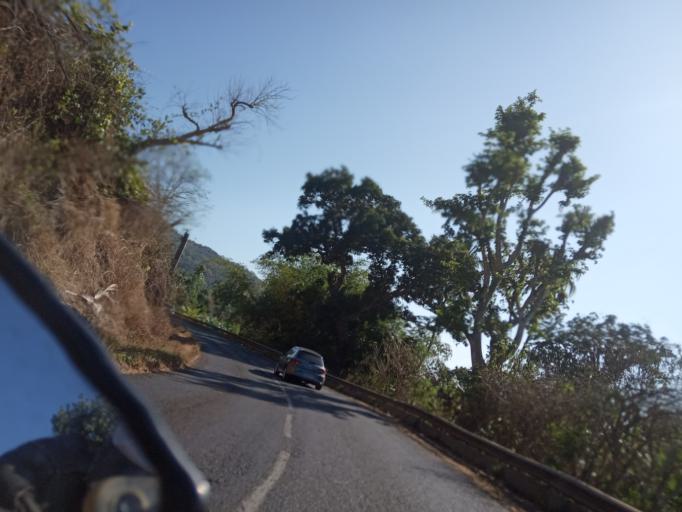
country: YT
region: Bandrele
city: Bandrele
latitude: -12.9026
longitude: 45.1936
